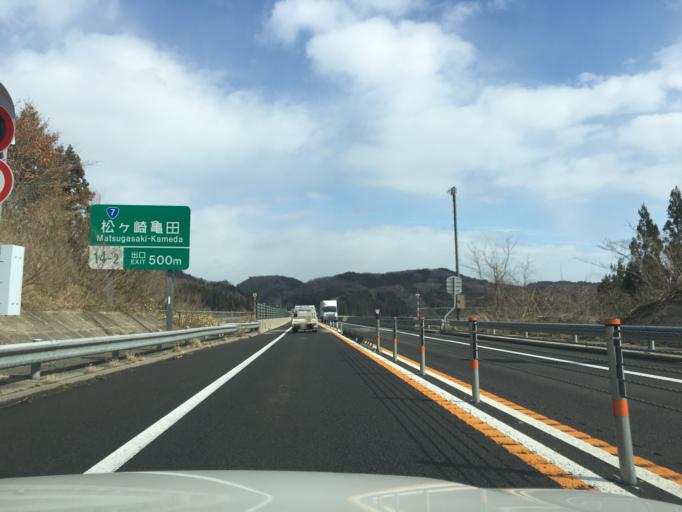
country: JP
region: Akita
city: Akita Shi
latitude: 39.4937
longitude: 140.0581
